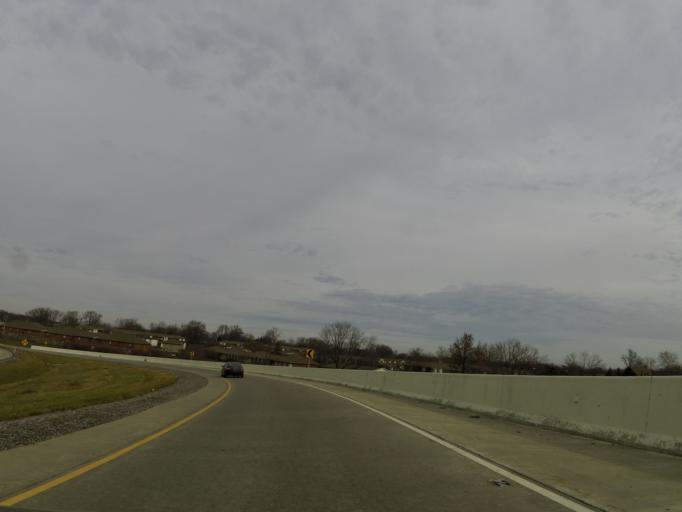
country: US
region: Indiana
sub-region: Marion County
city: Speedway
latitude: 39.8047
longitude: -86.2733
